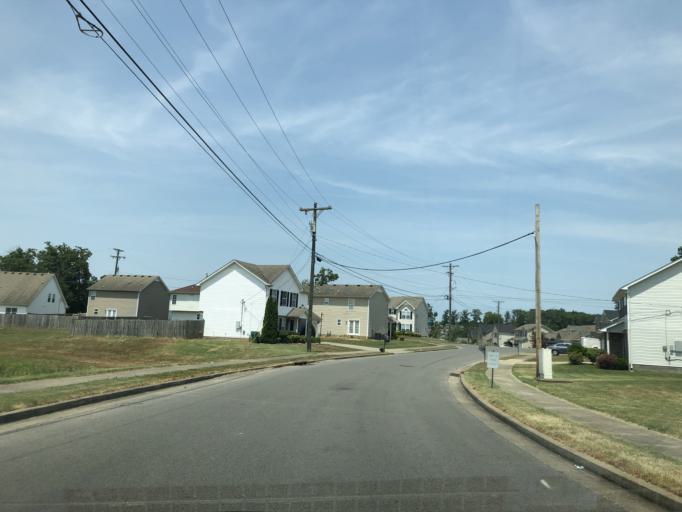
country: US
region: Tennessee
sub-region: Rutherford County
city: La Vergne
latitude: 36.0534
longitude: -86.6068
